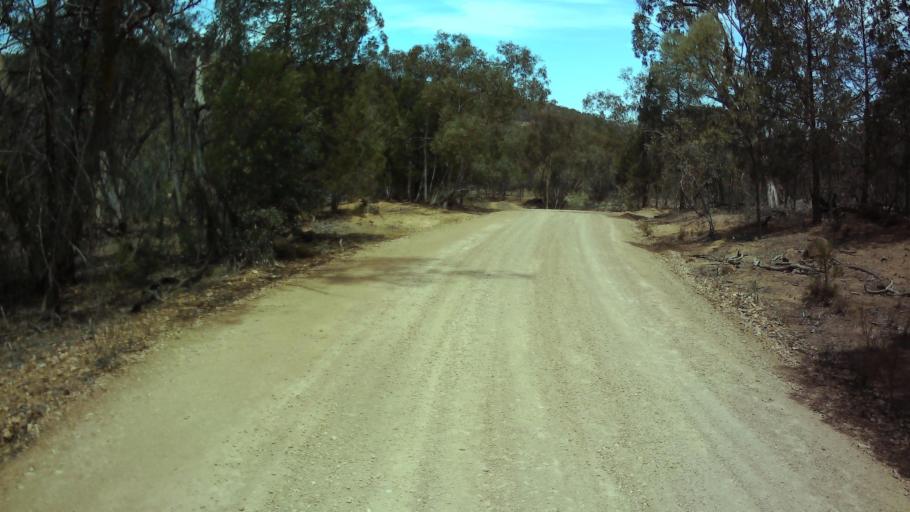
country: AU
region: New South Wales
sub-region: Weddin
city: Grenfell
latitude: -33.8140
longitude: 148.1631
